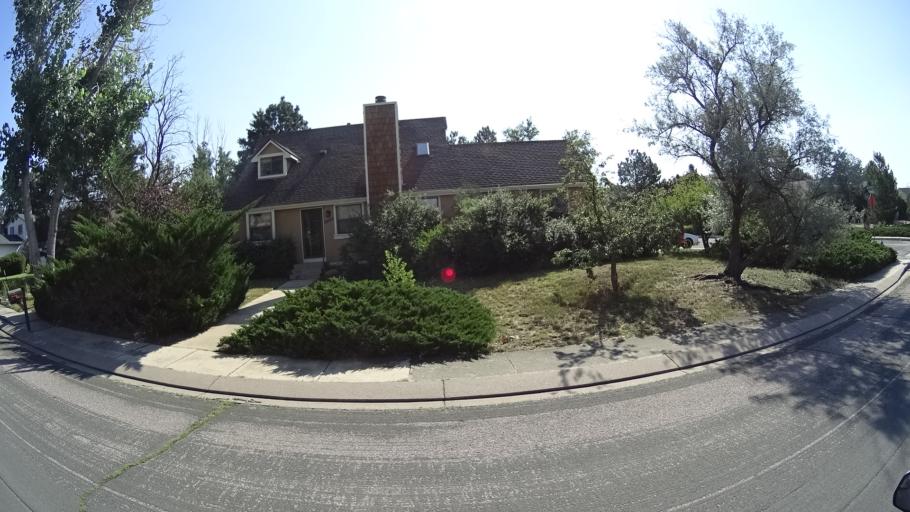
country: US
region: Colorado
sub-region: El Paso County
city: Air Force Academy
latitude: 38.9544
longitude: -104.7860
